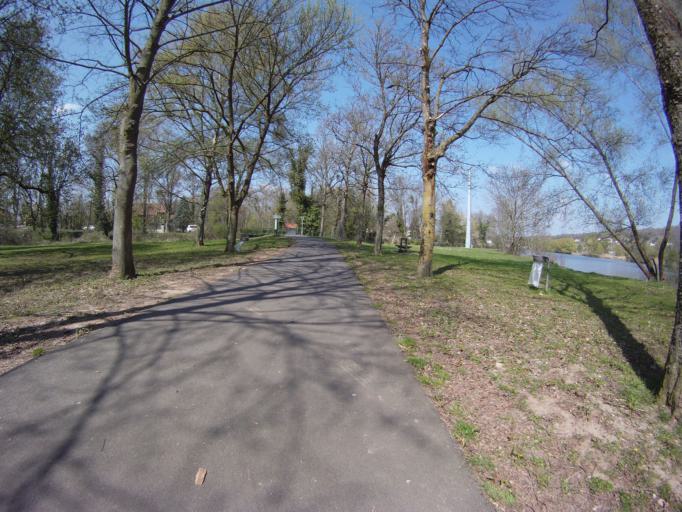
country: FR
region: Lorraine
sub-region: Departement de Meurthe-et-Moselle
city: Pont-a-Mousson
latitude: 48.8982
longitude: 6.0593
